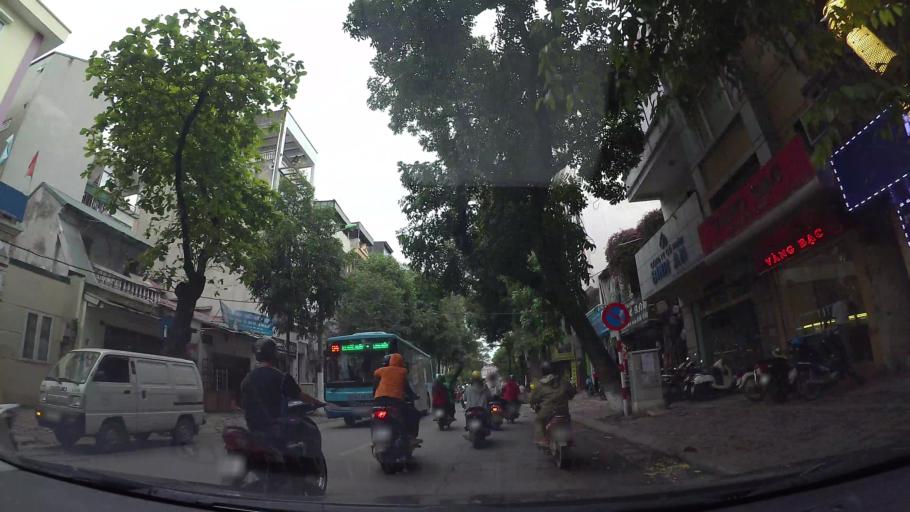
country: VN
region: Ha Noi
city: Hai BaTrung
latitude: 21.0106
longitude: 105.8600
